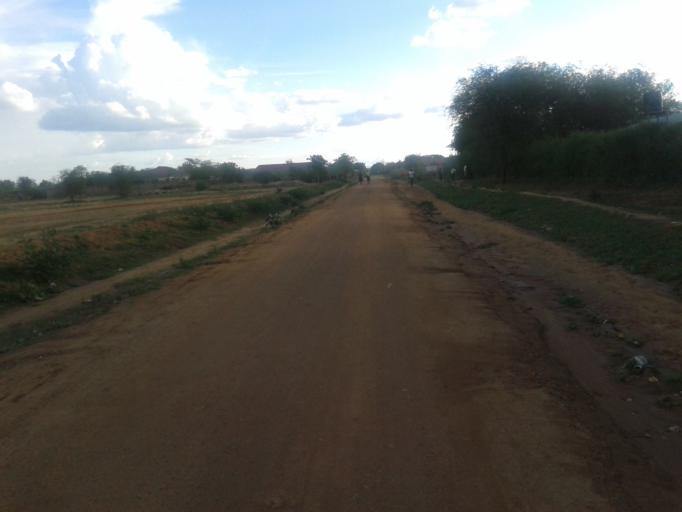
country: UG
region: Northern Region
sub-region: Kotido District
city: Kotido
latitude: 3.0017
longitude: 34.1088
